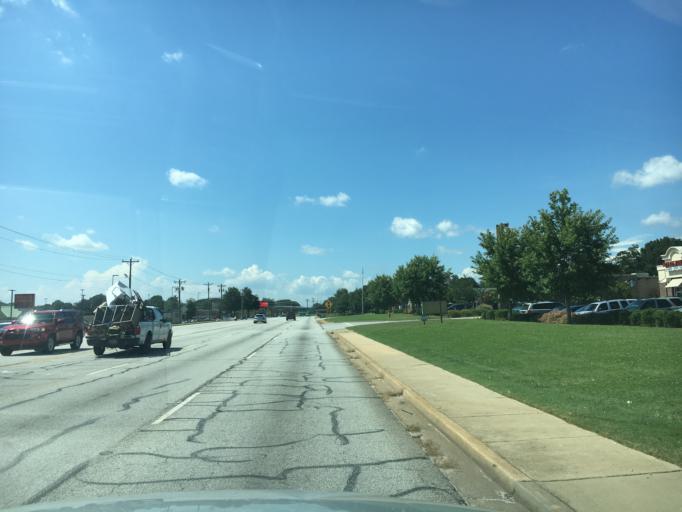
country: US
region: South Carolina
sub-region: Greenville County
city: Sans Souci
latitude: 34.8895
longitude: -82.3997
